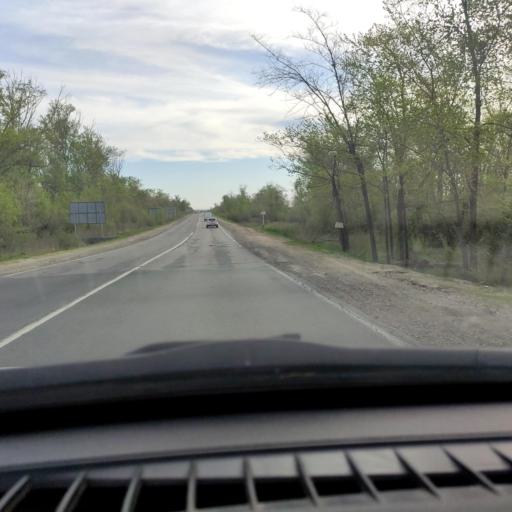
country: RU
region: Samara
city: Bereza
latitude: 53.4692
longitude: 50.1910
